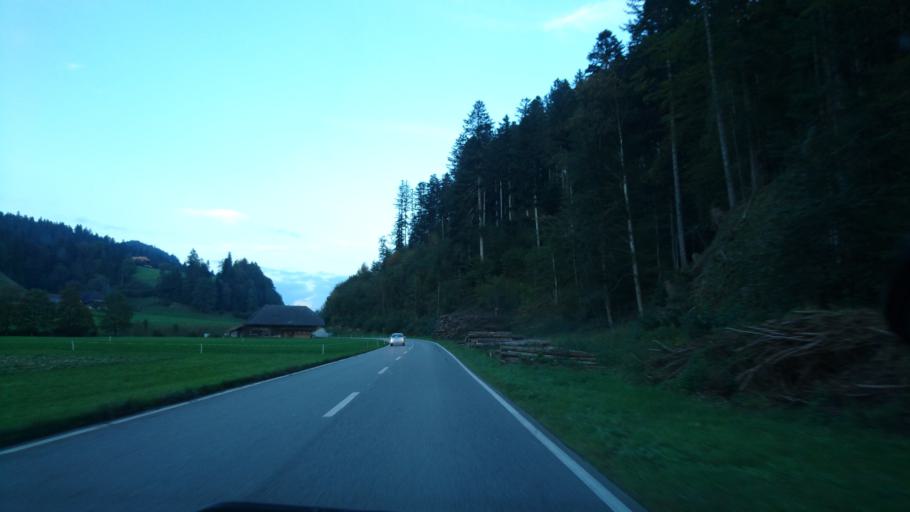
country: CH
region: Bern
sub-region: Emmental District
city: Trubschachen
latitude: 46.9272
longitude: 7.8532
